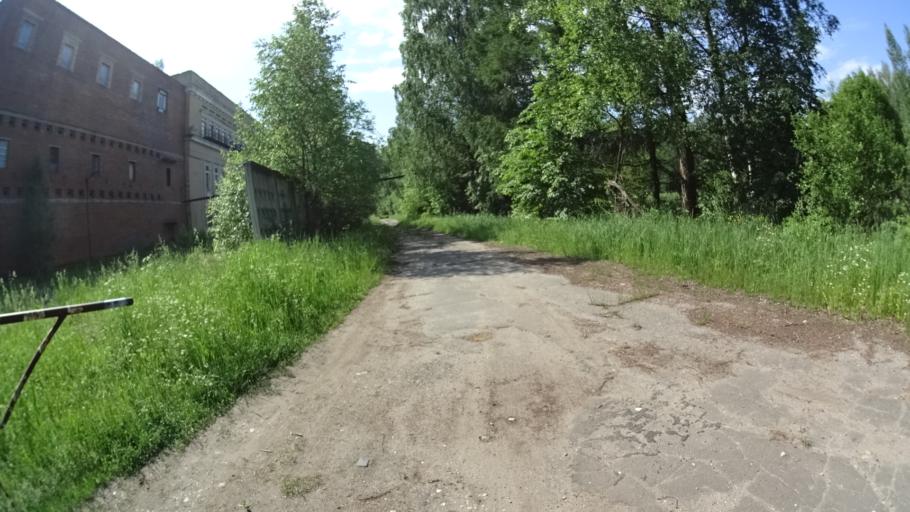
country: RU
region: Moskovskaya
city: Lesnoy
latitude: 56.0799
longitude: 37.9442
